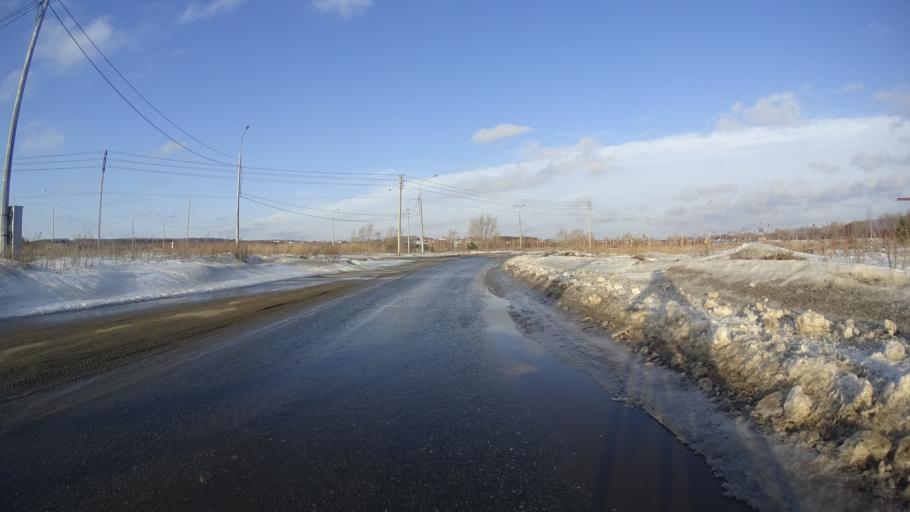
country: RU
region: Chelyabinsk
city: Sargazy
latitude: 55.1050
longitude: 61.2616
